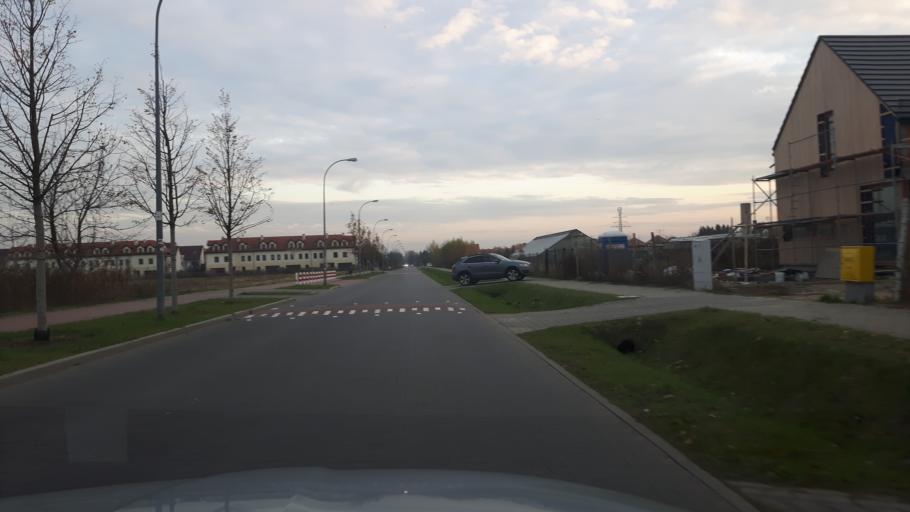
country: PL
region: Masovian Voivodeship
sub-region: Warszawa
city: Wilanow
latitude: 52.1789
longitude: 21.1076
